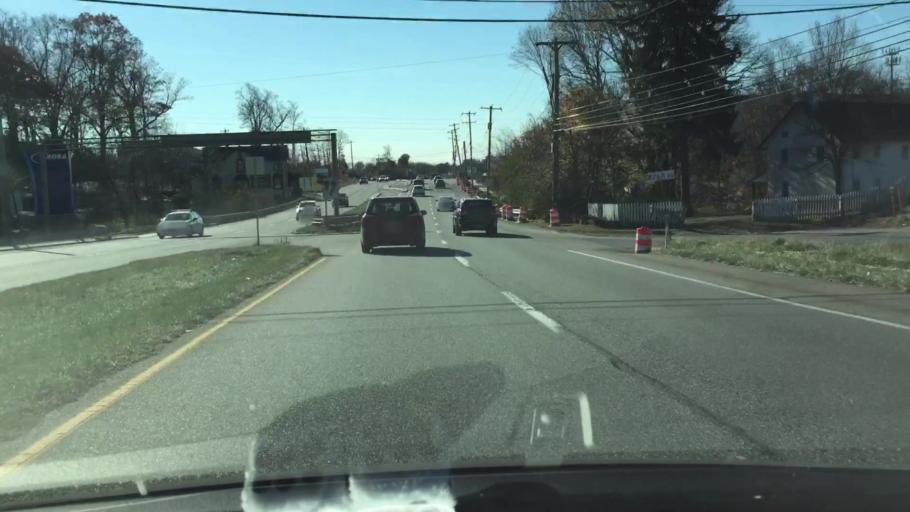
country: US
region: Pennsylvania
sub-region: Delaware County
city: Chester Heights
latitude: 39.8412
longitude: -75.5384
